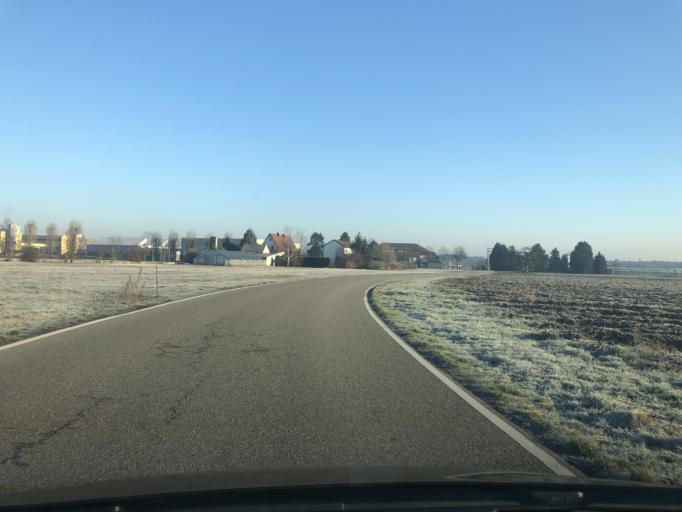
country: DE
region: Baden-Wuerttemberg
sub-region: Karlsruhe Region
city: Eggenstein-Leopoldshafen
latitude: 49.0719
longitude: 8.3995
